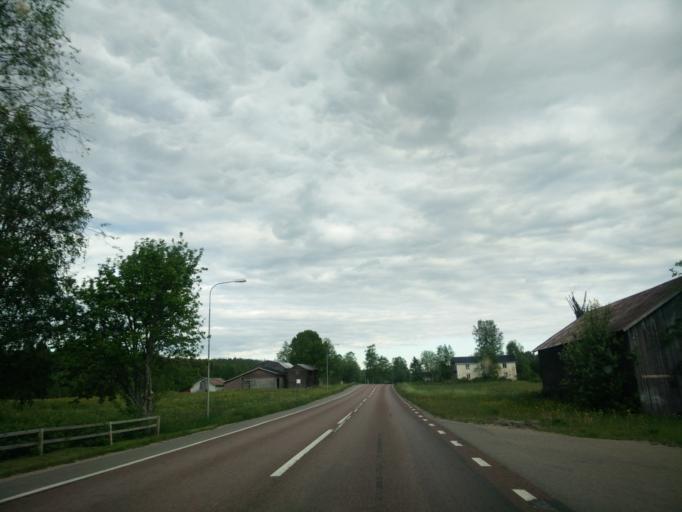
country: SE
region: Jaemtland
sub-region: Harjedalens Kommun
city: Sveg
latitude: 62.2809
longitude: 14.8038
